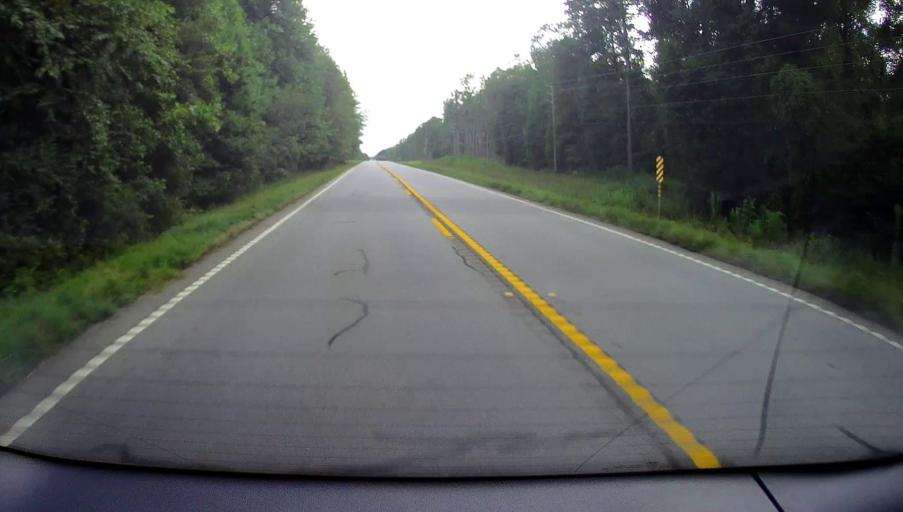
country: US
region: Georgia
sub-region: Meriwether County
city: Greenville
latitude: 33.0583
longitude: -84.5699
